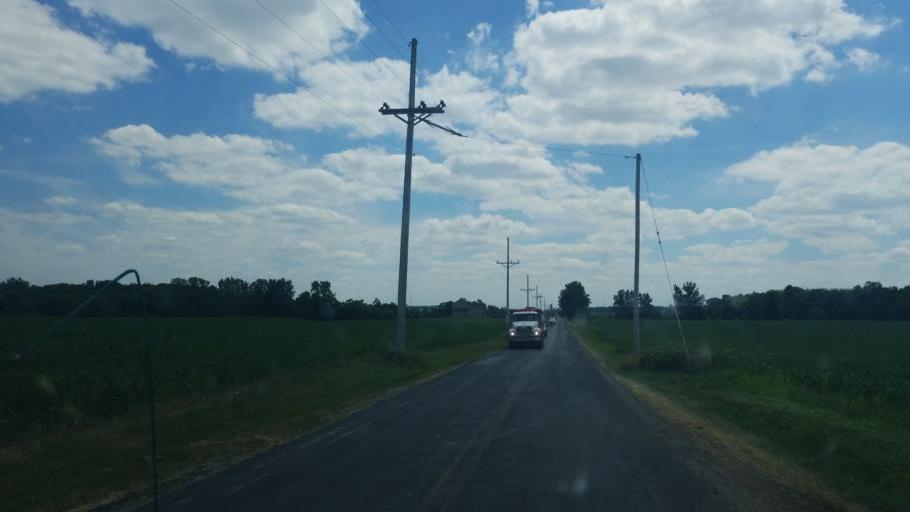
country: US
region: Ohio
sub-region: Williams County
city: Edgerton
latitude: 41.4662
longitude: -84.6912
